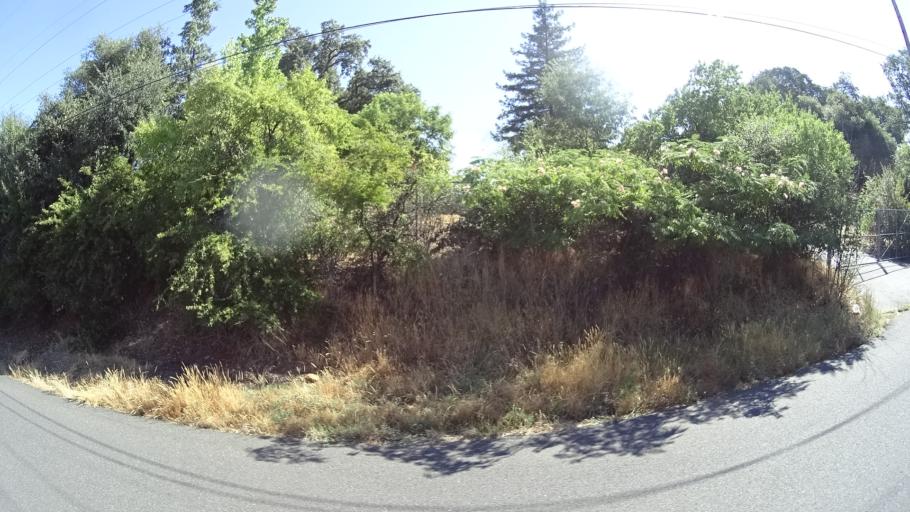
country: US
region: California
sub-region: Calaveras County
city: Angels Camp
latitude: 38.0737
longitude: -120.5530
